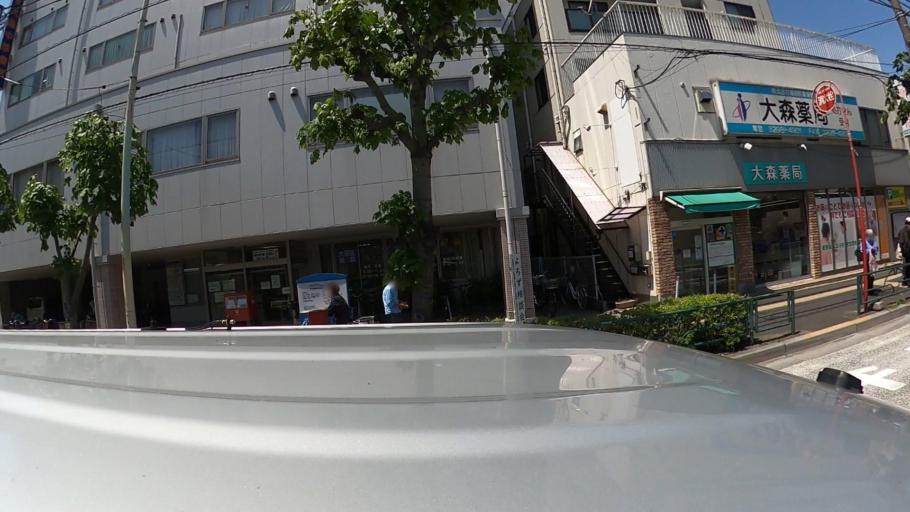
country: JP
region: Kanagawa
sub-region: Kawasaki-shi
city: Kawasaki
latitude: 35.5688
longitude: 139.7354
